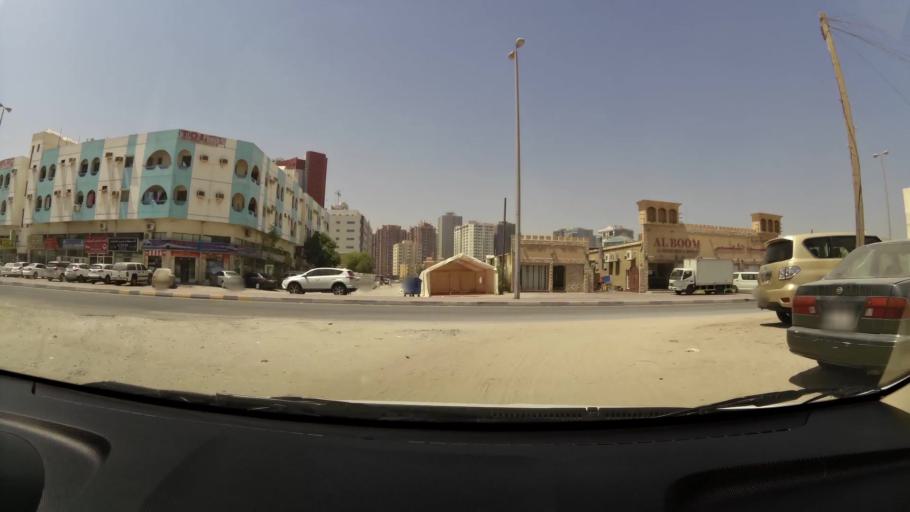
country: AE
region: Ajman
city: Ajman
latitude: 25.3922
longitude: 55.4612
